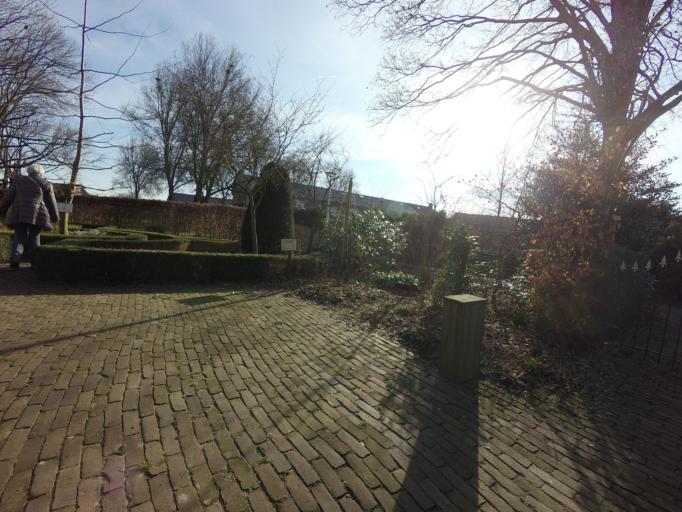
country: NL
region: Gelderland
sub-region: Gemeente Lochem
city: Lochem
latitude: 52.1614
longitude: 6.4118
